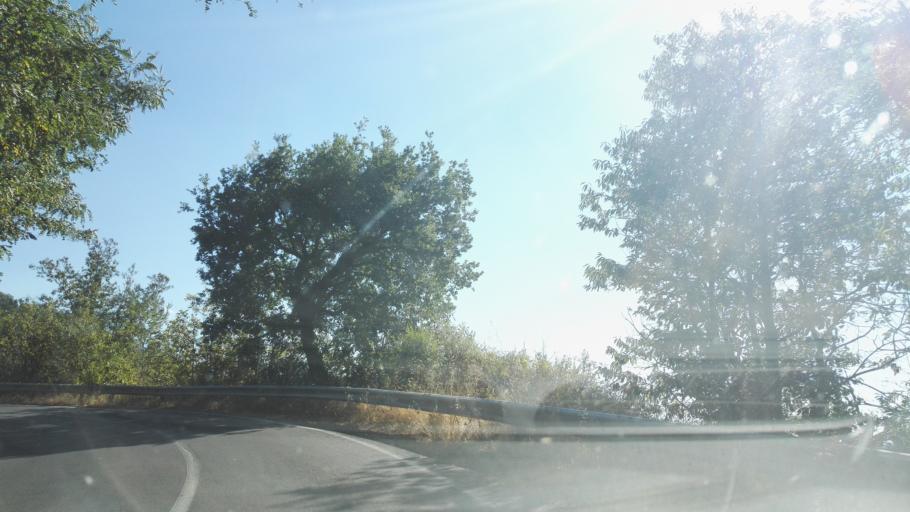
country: IT
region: Calabria
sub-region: Provincia di Vibo-Valentia
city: Sorianello
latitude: 38.5909
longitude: 16.2392
